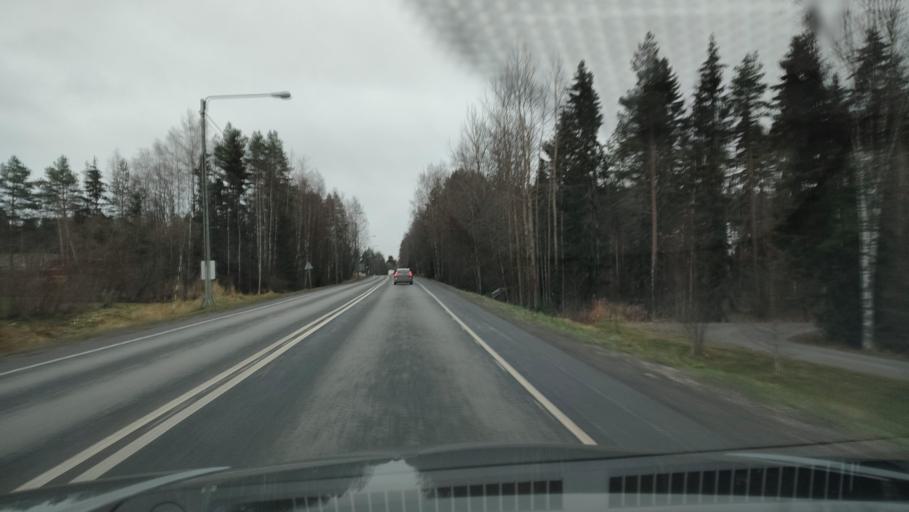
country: FI
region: Southern Ostrobothnia
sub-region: Seinaejoki
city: Ilmajoki
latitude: 62.7692
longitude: 22.6791
